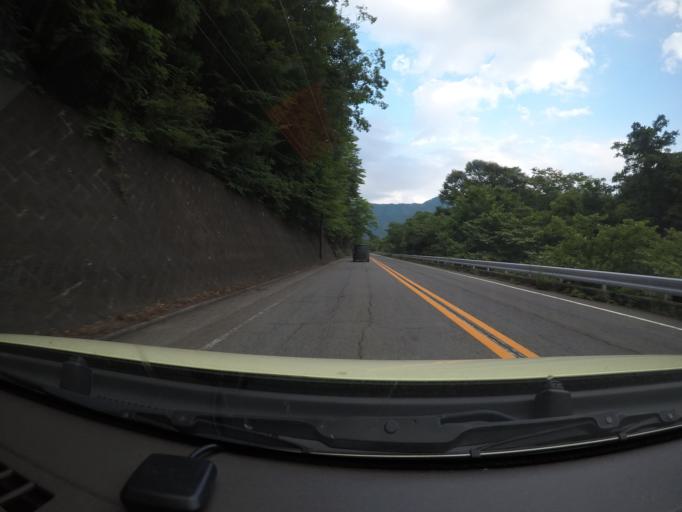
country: JP
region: Tochigi
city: Nikko
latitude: 36.7388
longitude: 139.5371
